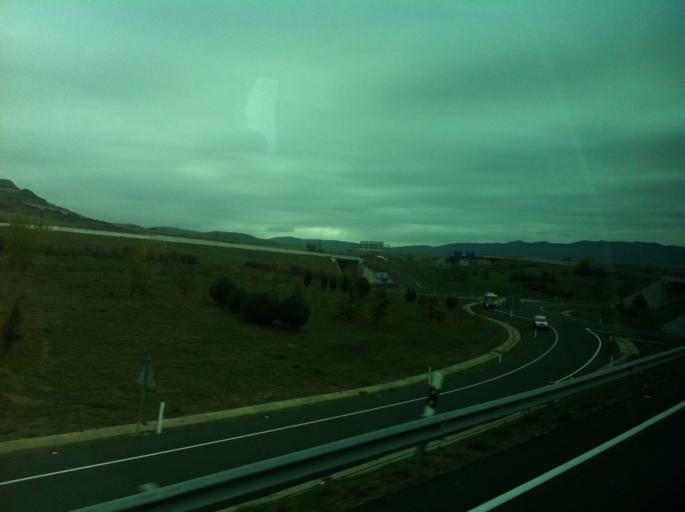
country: ES
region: Basque Country
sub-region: Provincia de Alava
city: Arminon
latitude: 42.7284
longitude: -2.8725
